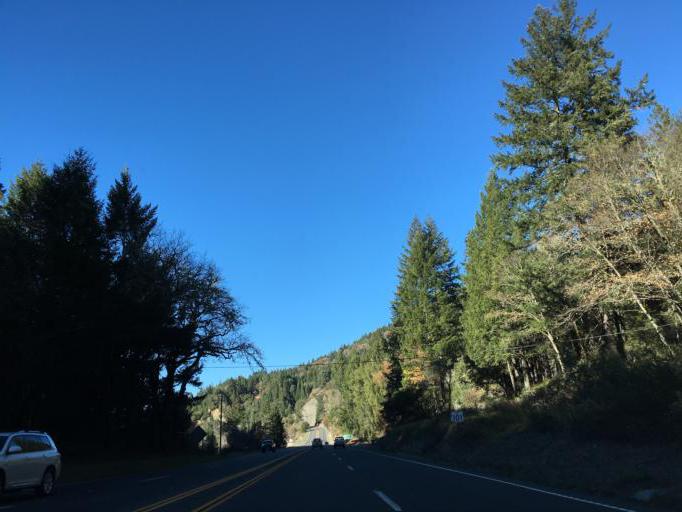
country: US
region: California
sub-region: Mendocino County
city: Brooktrails
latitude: 39.5159
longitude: -123.3904
